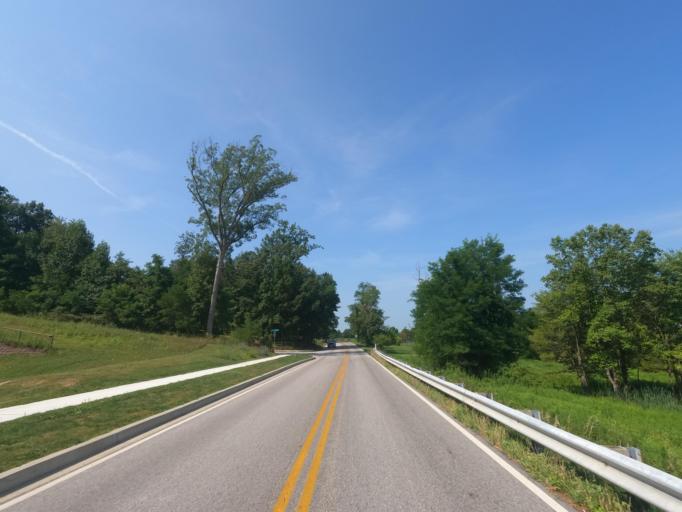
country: US
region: Maryland
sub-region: Carroll County
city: Westminster
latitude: 39.5960
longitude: -77.0190
